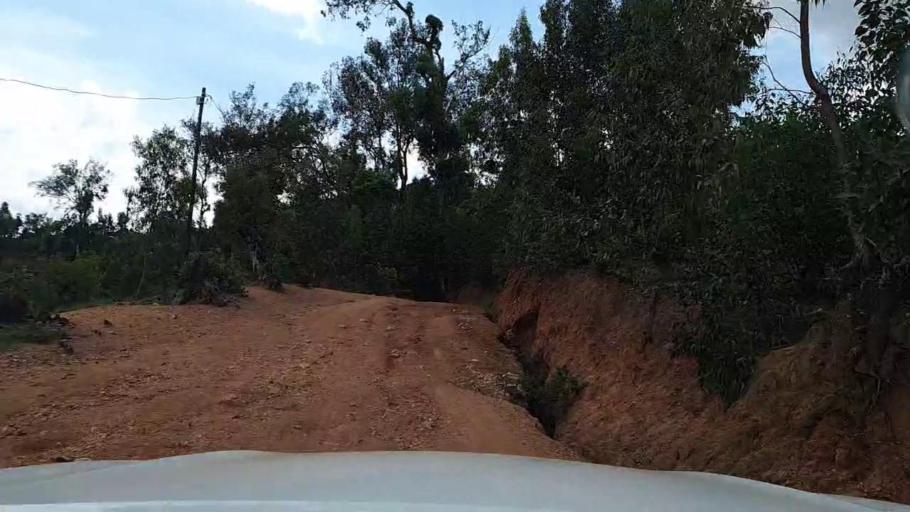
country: RW
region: Southern Province
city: Butare
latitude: -2.7530
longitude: 29.7548
